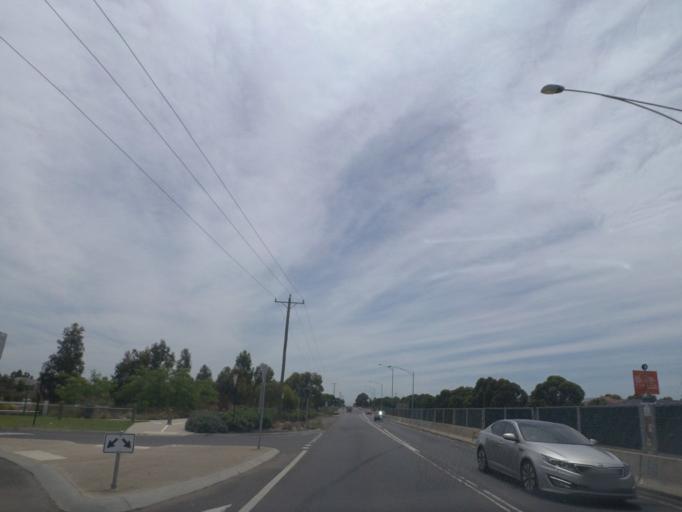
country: AU
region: Victoria
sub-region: Wyndham
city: Tarneit
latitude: -37.8467
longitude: 144.6885
